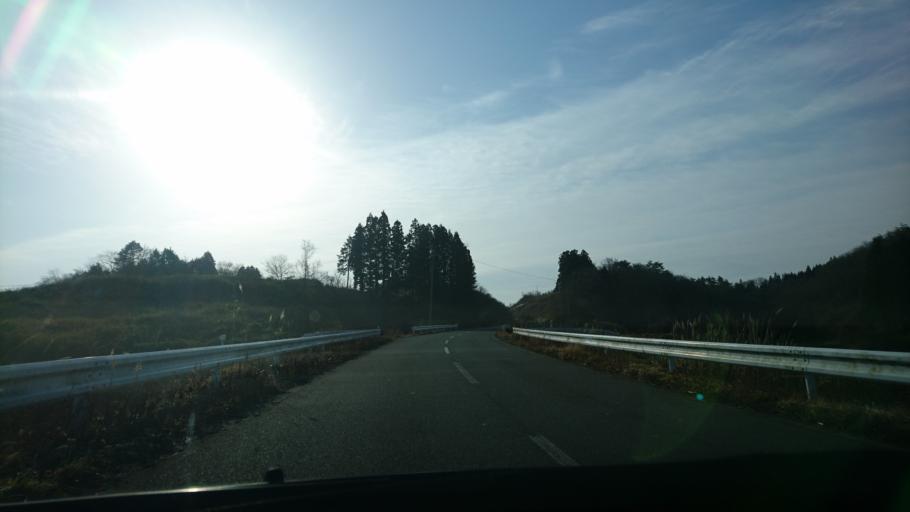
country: JP
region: Iwate
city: Ichinoseki
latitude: 38.8659
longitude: 141.1916
